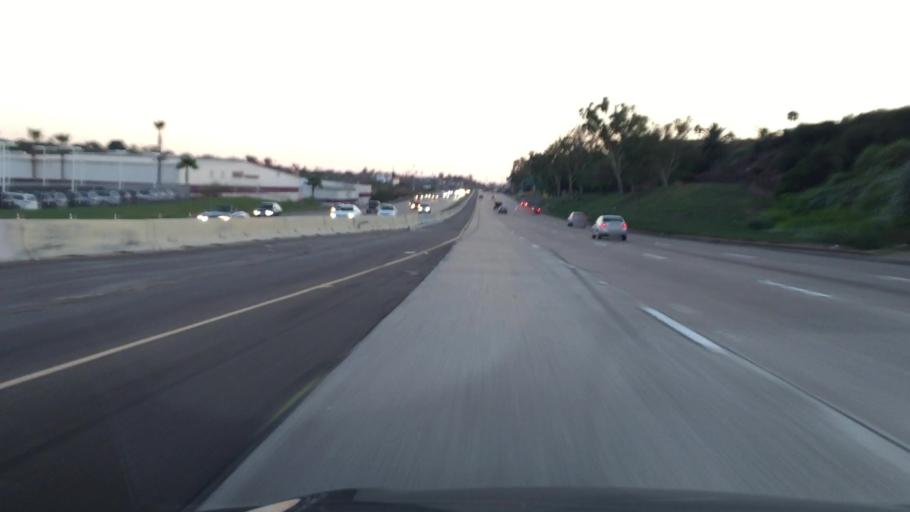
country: US
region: California
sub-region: San Diego County
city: Lemon Grove
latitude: 32.7400
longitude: -117.0531
